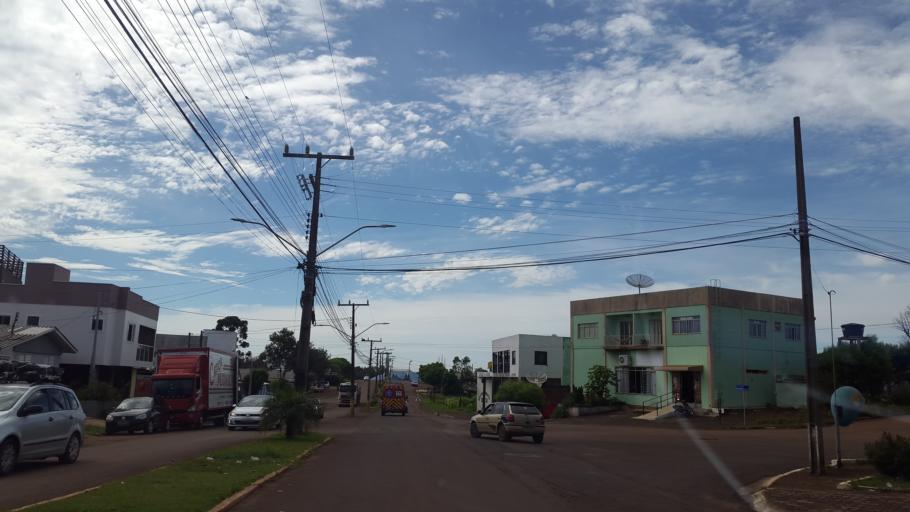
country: AR
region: Misiones
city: Bernardo de Irigoyen
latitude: -26.2638
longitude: -53.6284
